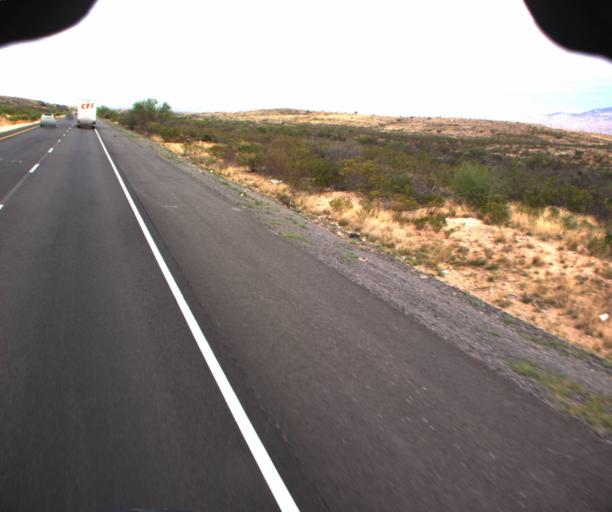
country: US
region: Arizona
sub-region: Cochise County
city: Mescal
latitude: 31.9690
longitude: -110.4706
